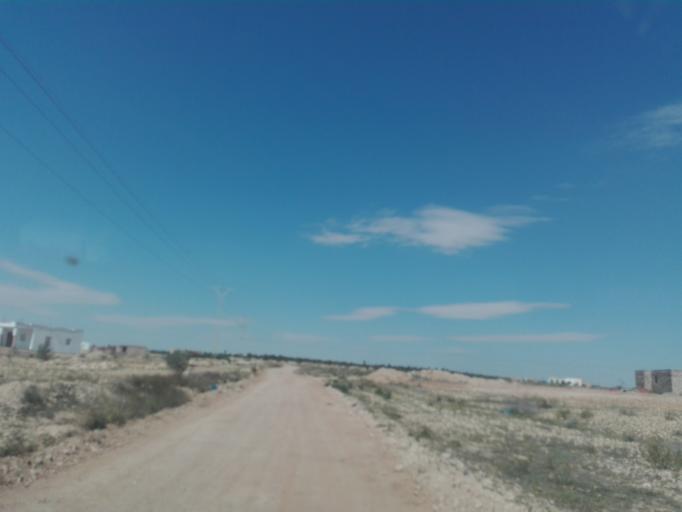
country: TN
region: Safaqis
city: Sfax
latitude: 34.6884
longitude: 10.5339
